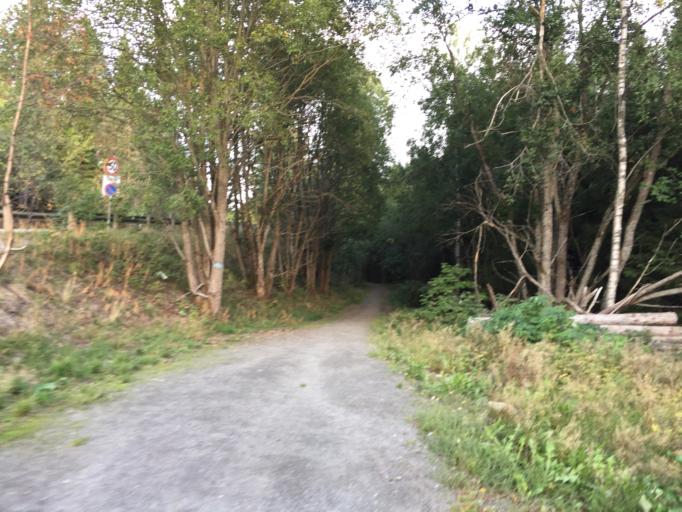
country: NO
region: Akershus
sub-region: Raelingen
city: Fjerdingby
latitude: 59.9292
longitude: 11.0403
